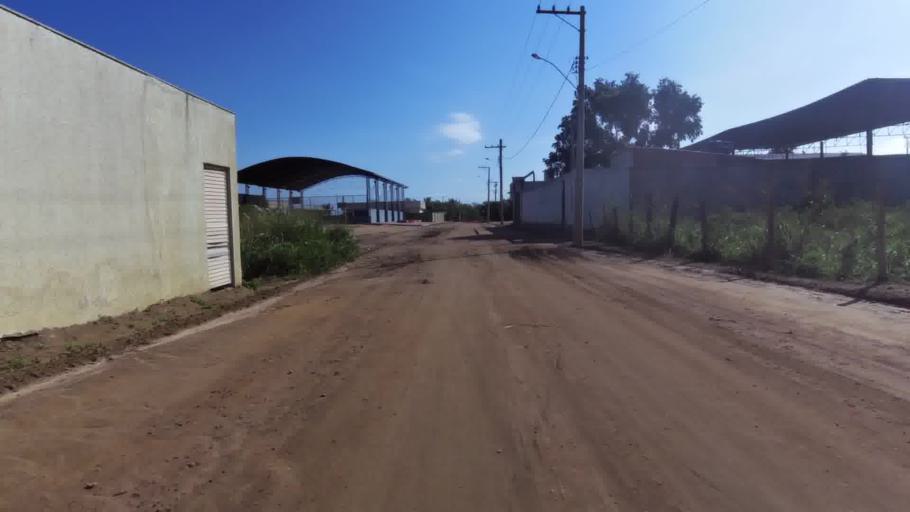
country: BR
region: Espirito Santo
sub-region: Piuma
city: Piuma
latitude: -20.8242
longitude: -40.6230
